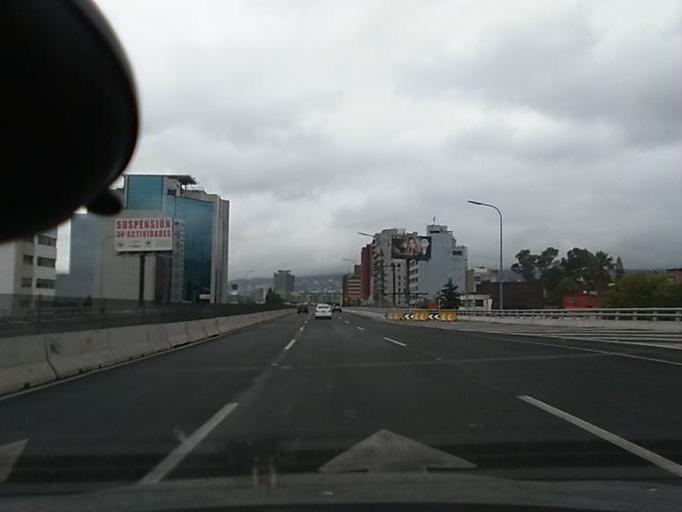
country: MX
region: Mexico City
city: Magdalena Contreras
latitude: 19.3187
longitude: -99.2215
